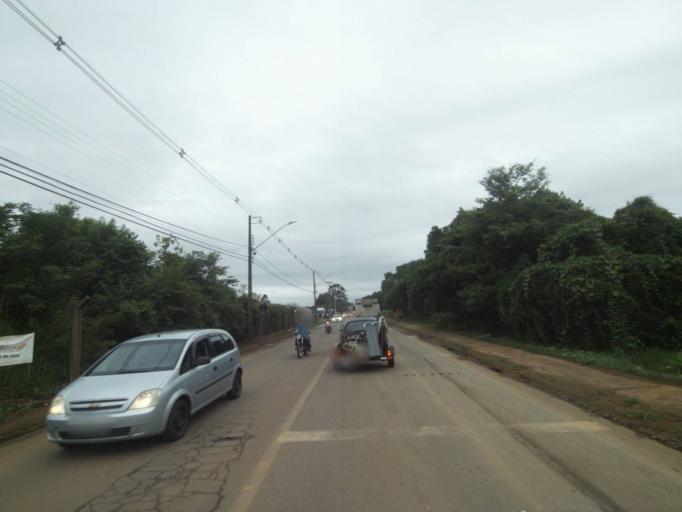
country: BR
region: Parana
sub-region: Telemaco Borba
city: Telemaco Borba
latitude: -24.3269
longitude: -50.6529
